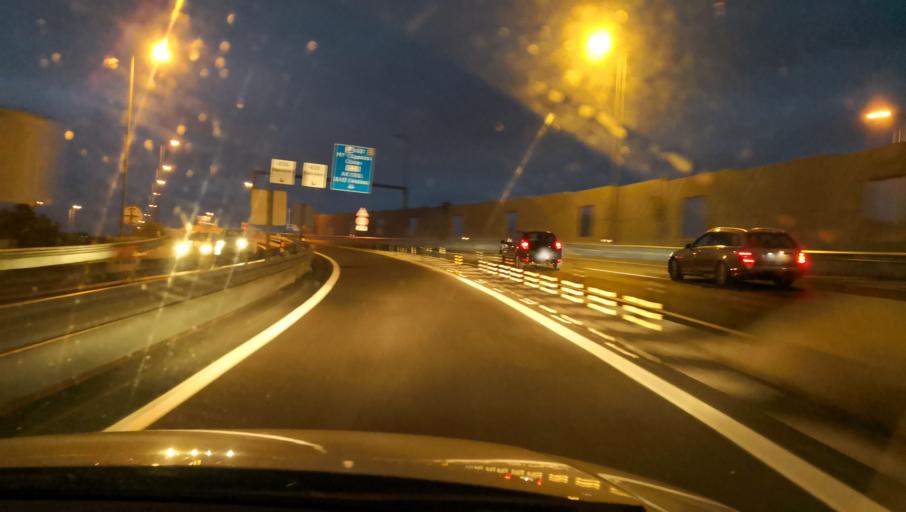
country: PT
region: Setubal
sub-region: Barreiro
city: Santo Antonio da Charneca
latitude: 38.6026
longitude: -9.0190
